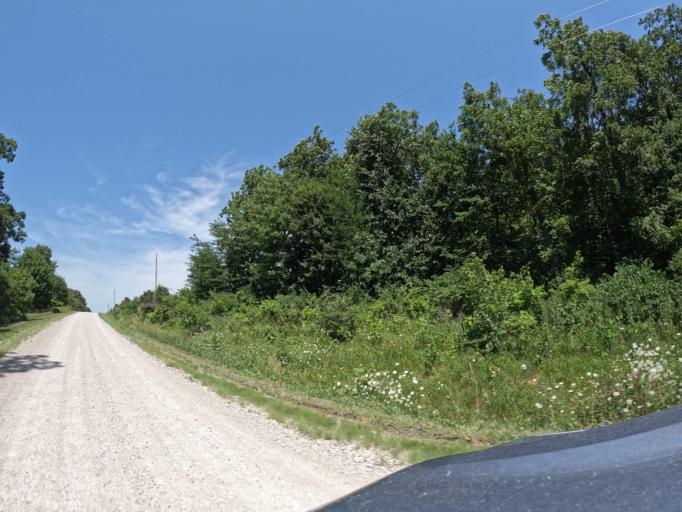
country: US
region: Iowa
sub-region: Henry County
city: Mount Pleasant
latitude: 40.9892
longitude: -91.6362
